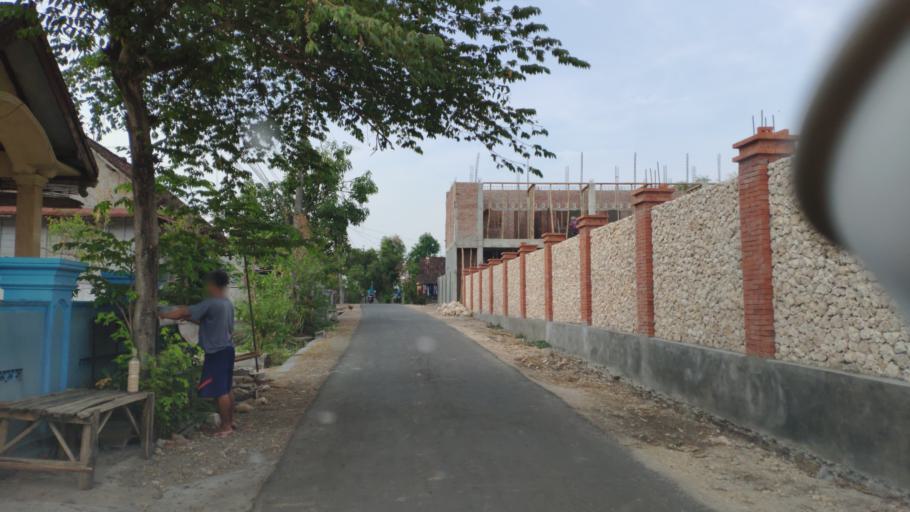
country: ID
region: Central Java
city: Tutup
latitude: -6.9682
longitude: 111.3924
